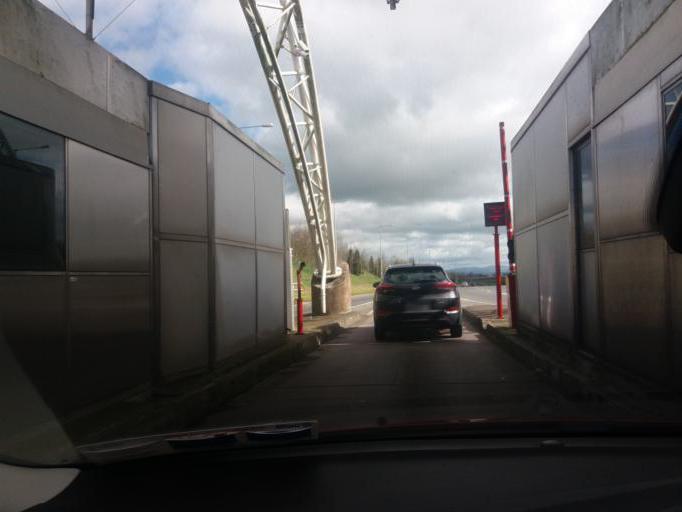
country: IE
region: Munster
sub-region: County Cork
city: Watergrasshill
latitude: 52.0271
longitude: -8.3285
